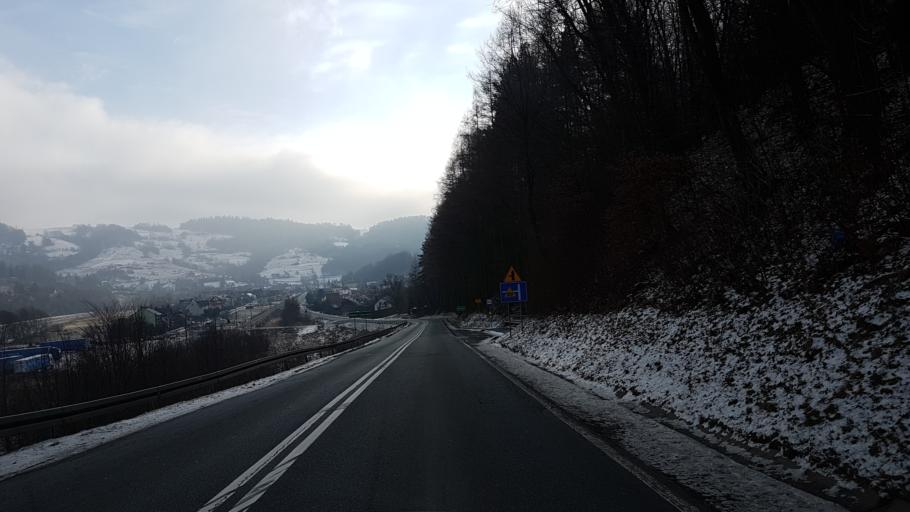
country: PL
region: Lesser Poland Voivodeship
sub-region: Powiat nowosadecki
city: Rytro
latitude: 49.4740
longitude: 20.6854
